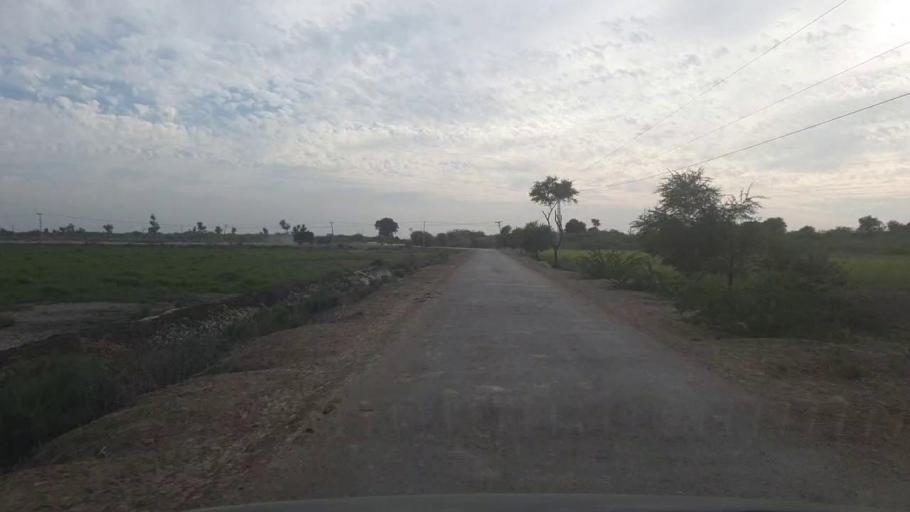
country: PK
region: Sindh
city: Samaro
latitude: 25.3243
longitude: 69.2356
